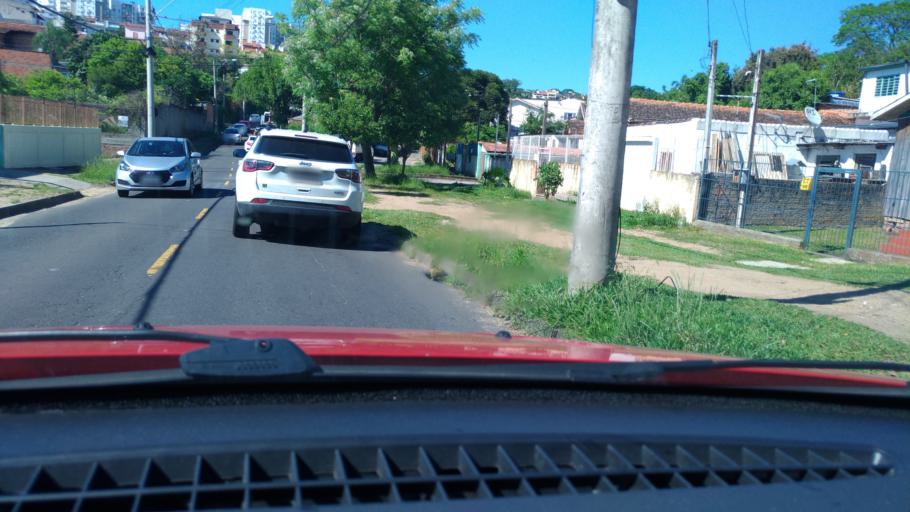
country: BR
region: Rio Grande do Sul
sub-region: Porto Alegre
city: Porto Alegre
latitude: -30.0310
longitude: -51.1477
